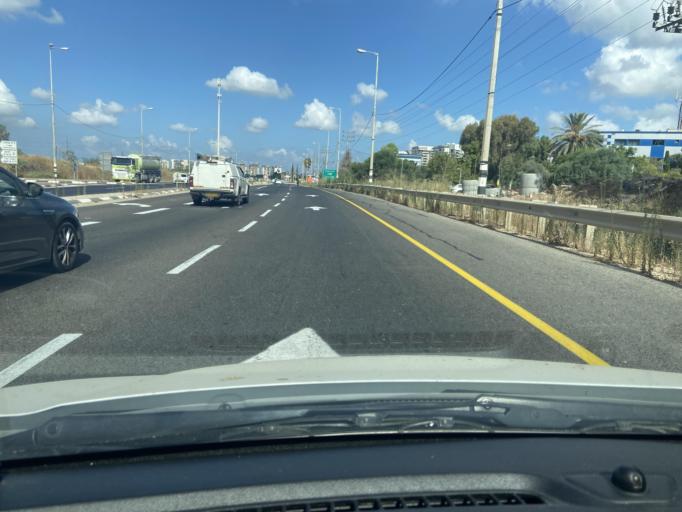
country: IL
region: Central District
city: Yehud
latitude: 32.0263
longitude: 34.8944
